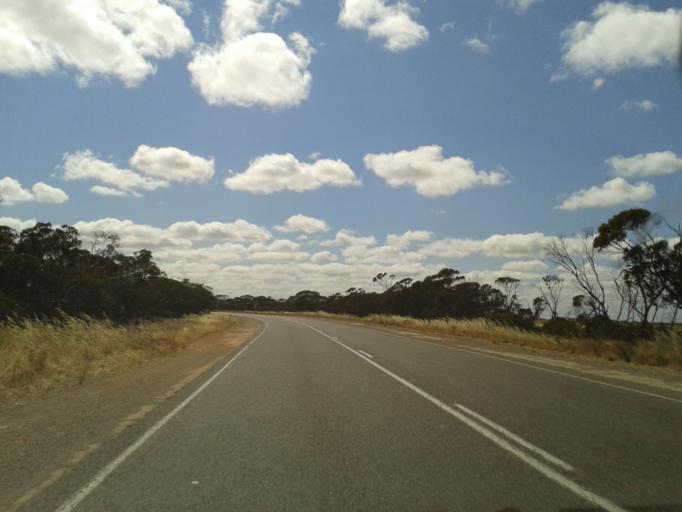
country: AU
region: South Australia
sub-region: Loxton Waikerie
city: Loxton
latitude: -35.2785
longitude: 140.9007
